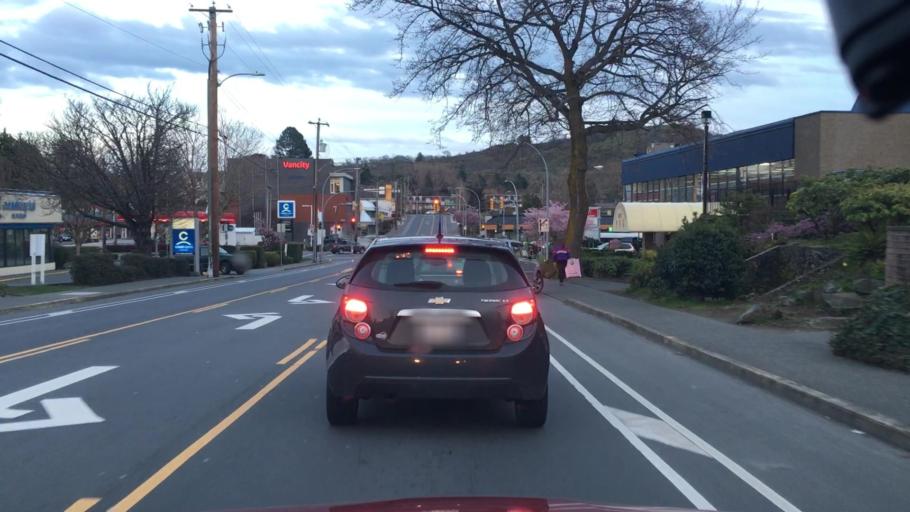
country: CA
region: British Columbia
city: Oak Bay
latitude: 48.4618
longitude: -123.3344
